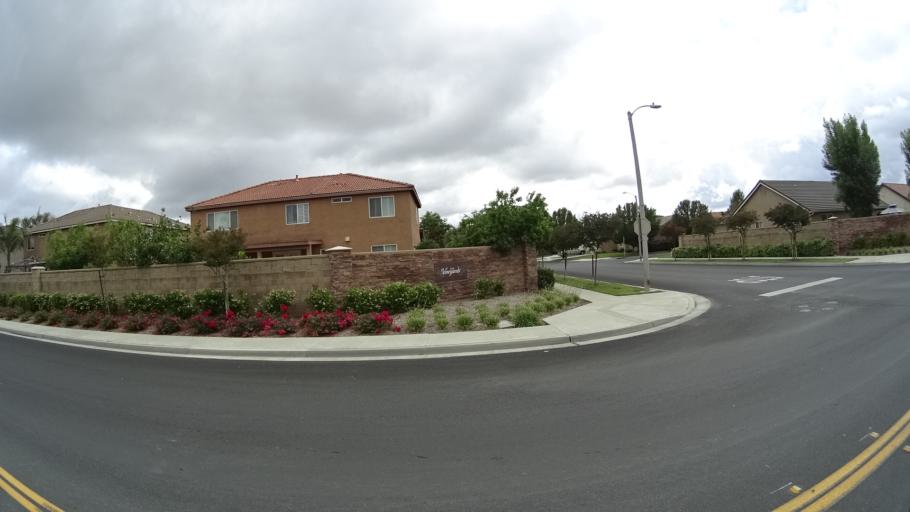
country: US
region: California
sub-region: Kings County
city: Lucerne
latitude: 36.3512
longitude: -119.6685
